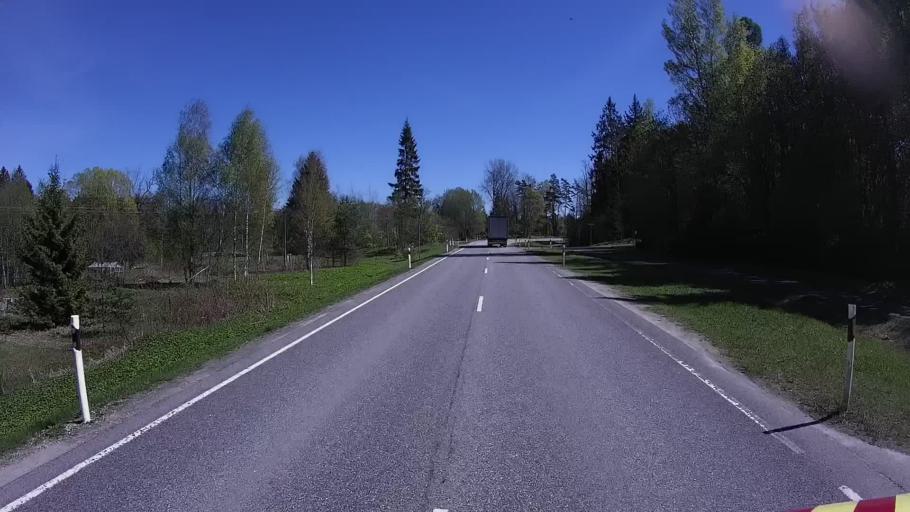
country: EE
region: Harju
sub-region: Kuusalu vald
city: Kuusalu
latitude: 59.2680
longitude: 25.6547
